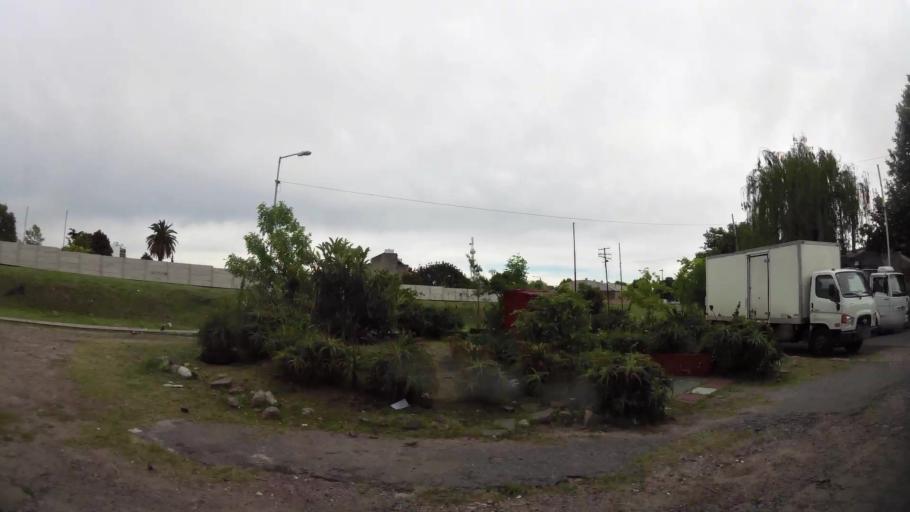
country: AR
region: Buenos Aires
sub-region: Partido de Avellaneda
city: Avellaneda
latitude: -34.6634
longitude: -58.3567
